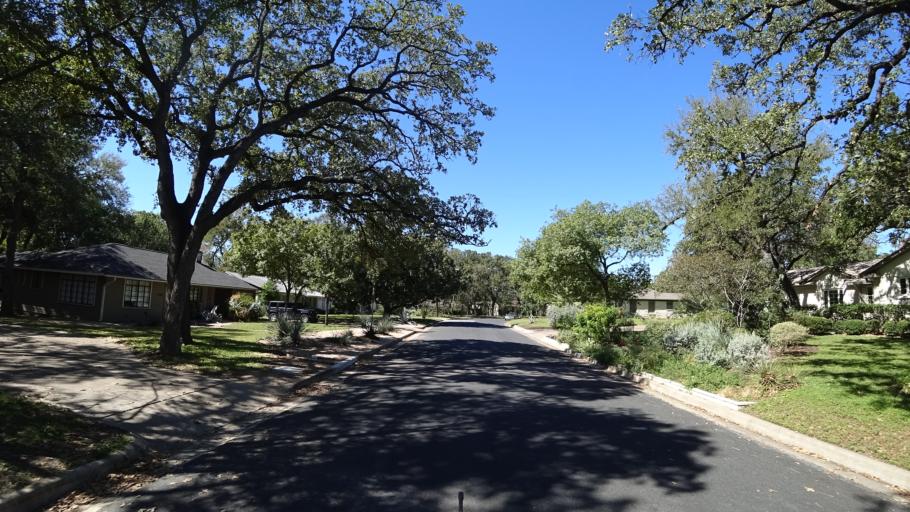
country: US
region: Texas
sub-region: Travis County
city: Austin
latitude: 30.2965
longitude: -97.7155
